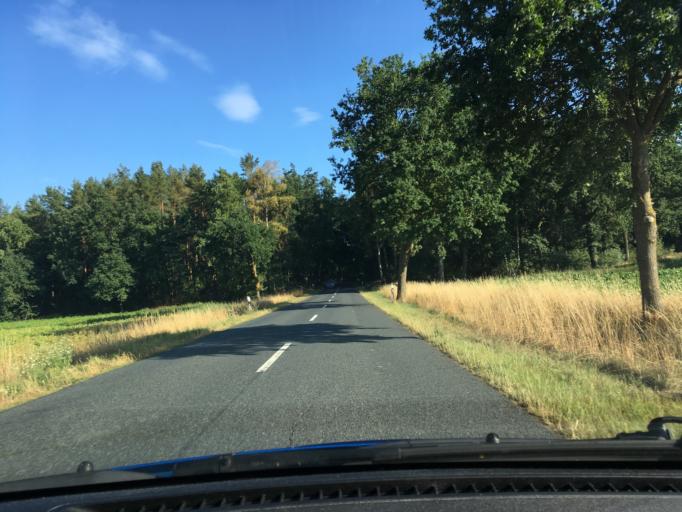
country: DE
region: Lower Saxony
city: Dahlenburg
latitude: 53.2092
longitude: 10.7068
